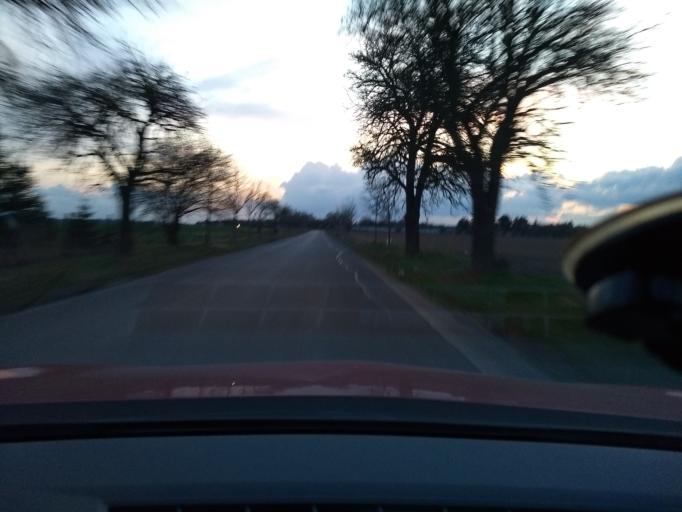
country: CZ
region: Central Bohemia
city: Jenec
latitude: 50.0688
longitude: 14.2147
